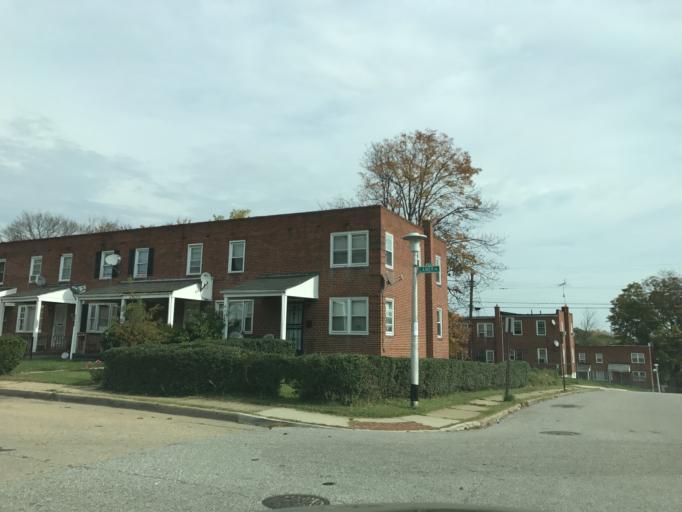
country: US
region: Maryland
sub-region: Baltimore County
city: Lochearn
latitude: 39.3434
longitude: -76.6620
